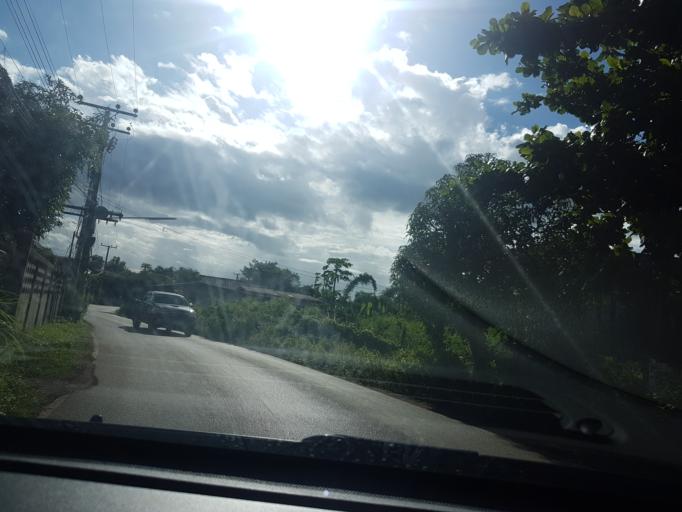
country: TH
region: Lampang
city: Ko Kha
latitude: 18.2333
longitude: 99.4261
